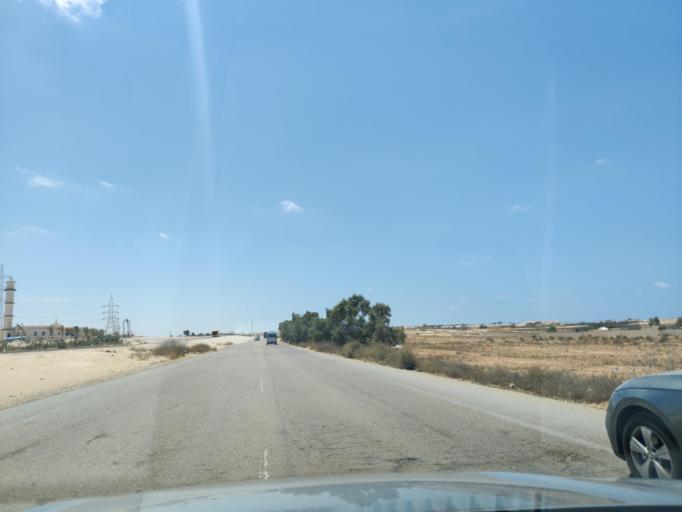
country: EG
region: Muhafazat Matruh
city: Al `Alamayn
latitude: 31.0694
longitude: 28.1629
